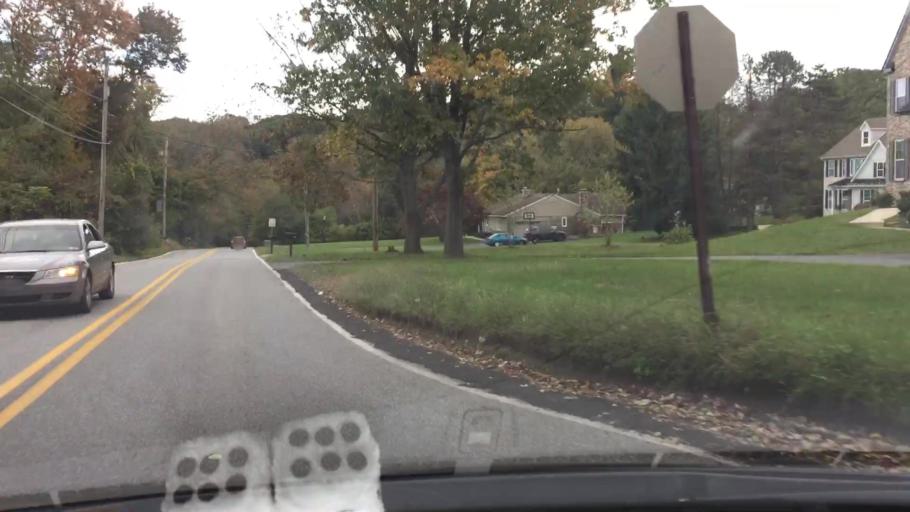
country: US
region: Pennsylvania
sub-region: Delaware County
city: Lima
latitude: 39.9295
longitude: -75.4270
